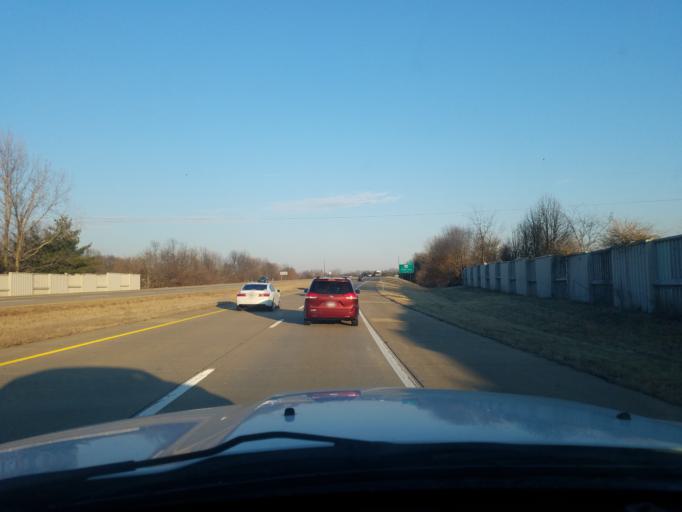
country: US
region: Indiana
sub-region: Warrick County
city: Newburgh
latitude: 37.9493
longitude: -87.4650
